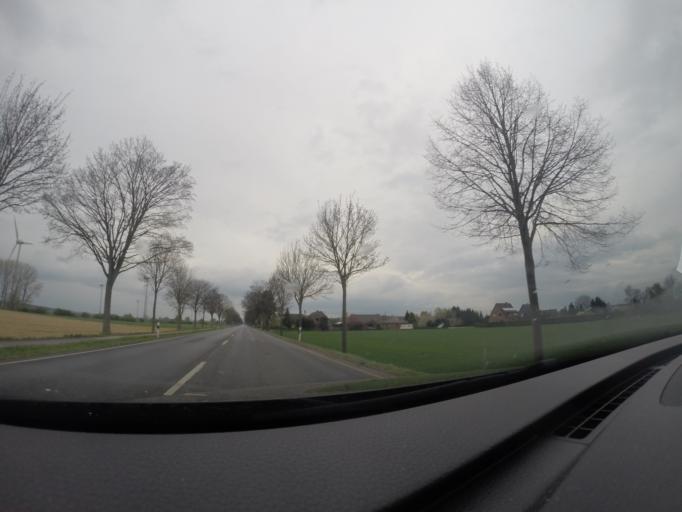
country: DE
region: North Rhine-Westphalia
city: Rheinberg
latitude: 51.5690
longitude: 6.5715
